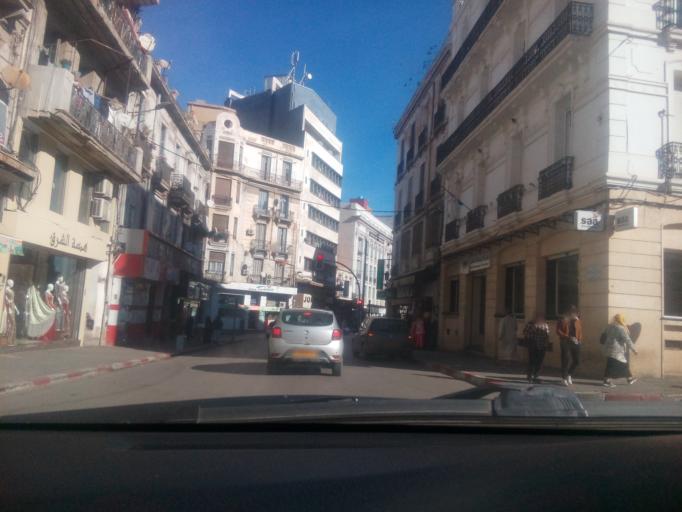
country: DZ
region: Oran
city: Oran
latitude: 35.7011
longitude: -0.6468
